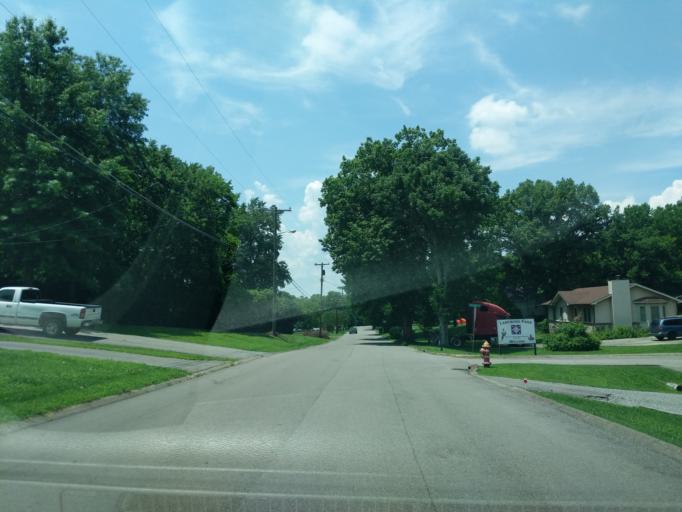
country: US
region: Tennessee
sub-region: Davidson County
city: Lakewood
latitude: 36.2385
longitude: -86.6345
